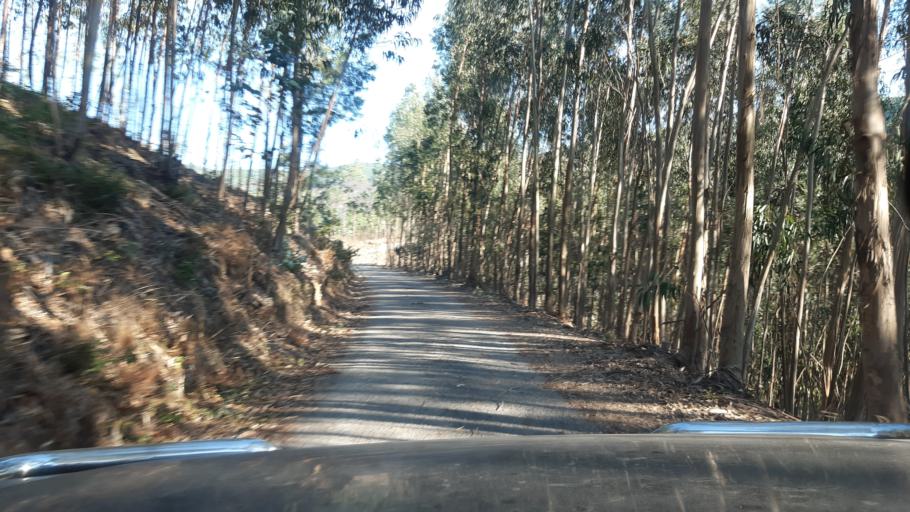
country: PT
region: Viseu
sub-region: Mortagua
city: Mortagua
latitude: 40.5262
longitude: -8.2551
